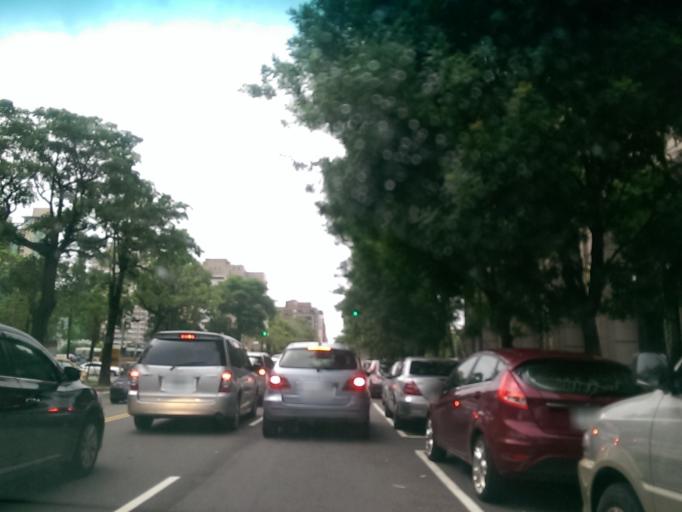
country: TW
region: Taiwan
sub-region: Taichung City
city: Taichung
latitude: 24.1468
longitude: 120.6432
